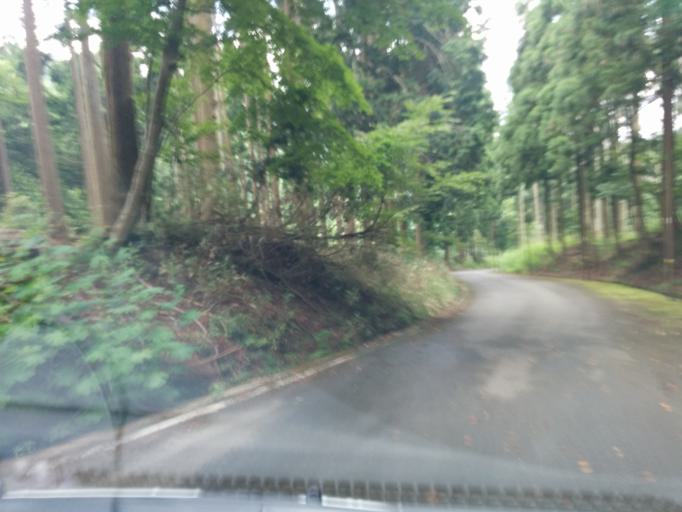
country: JP
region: Kyoto
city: Miyazu
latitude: 35.4575
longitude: 135.1122
